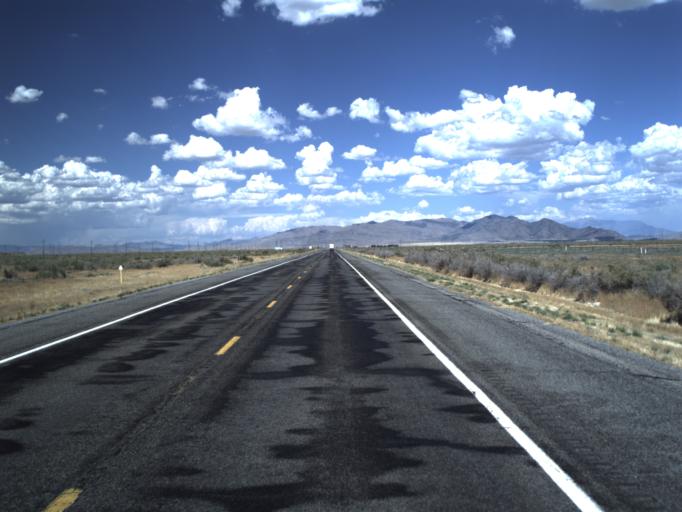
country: US
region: Utah
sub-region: Millard County
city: Delta
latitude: 39.4544
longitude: -112.4410
